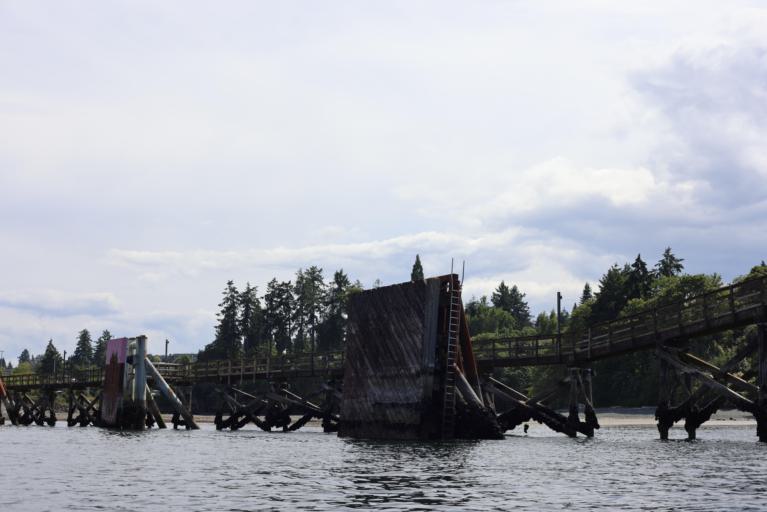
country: CA
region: British Columbia
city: Nanaimo
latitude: 49.1958
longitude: -123.9582
